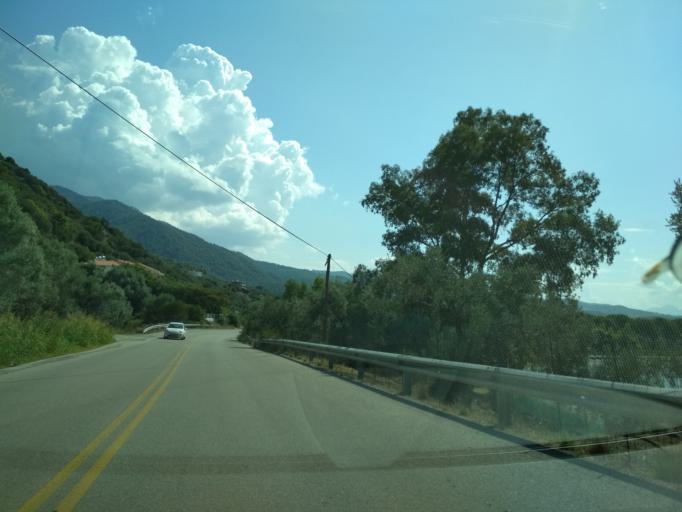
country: GR
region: Central Greece
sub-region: Nomos Evvoias
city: Roviai
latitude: 38.8312
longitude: 23.2026
